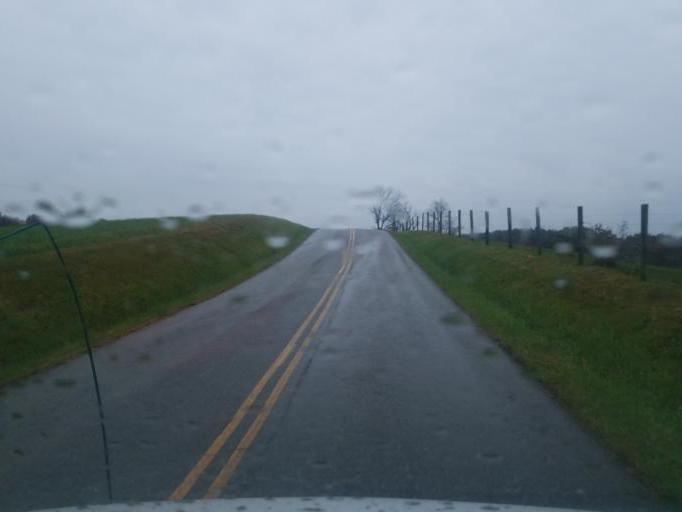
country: US
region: Ohio
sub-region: Washington County
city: Beverly
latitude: 39.4396
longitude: -81.6203
